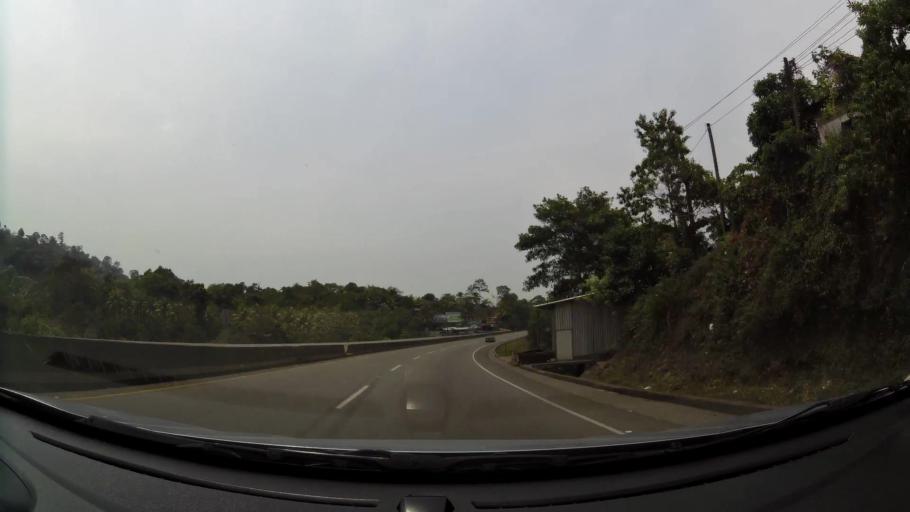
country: HN
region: Cortes
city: Oropendolas
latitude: 14.9913
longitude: -87.9308
